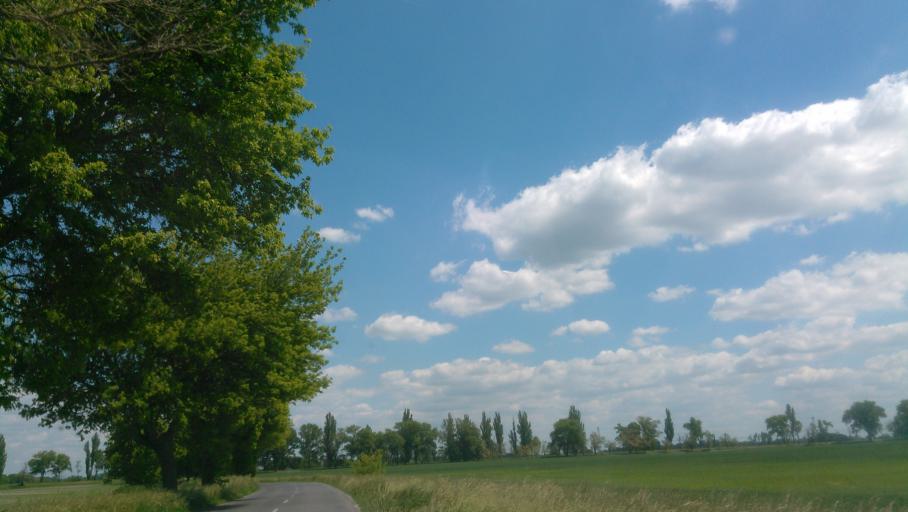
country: SK
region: Trnavsky
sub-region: Okres Dunajska Streda
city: Velky Meder
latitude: 47.9104
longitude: 17.7663
